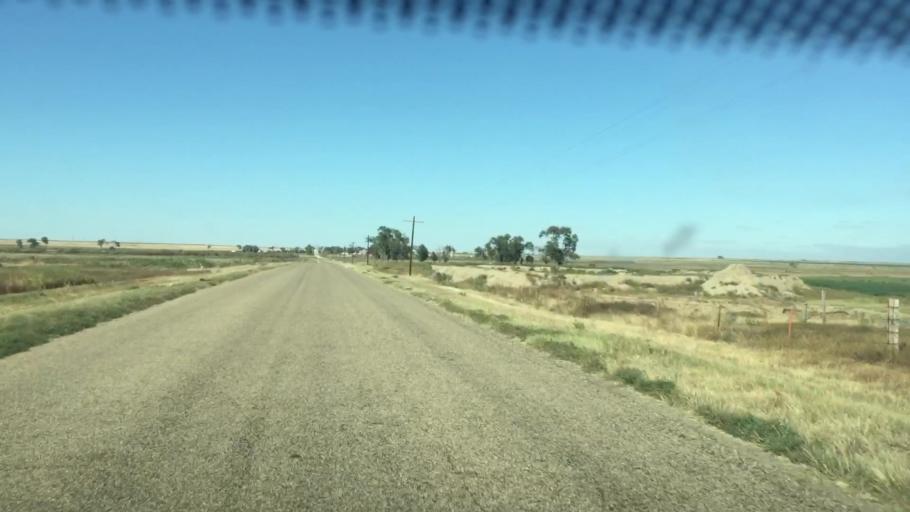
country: US
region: Colorado
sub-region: Prowers County
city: Lamar
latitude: 38.1054
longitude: -102.5214
